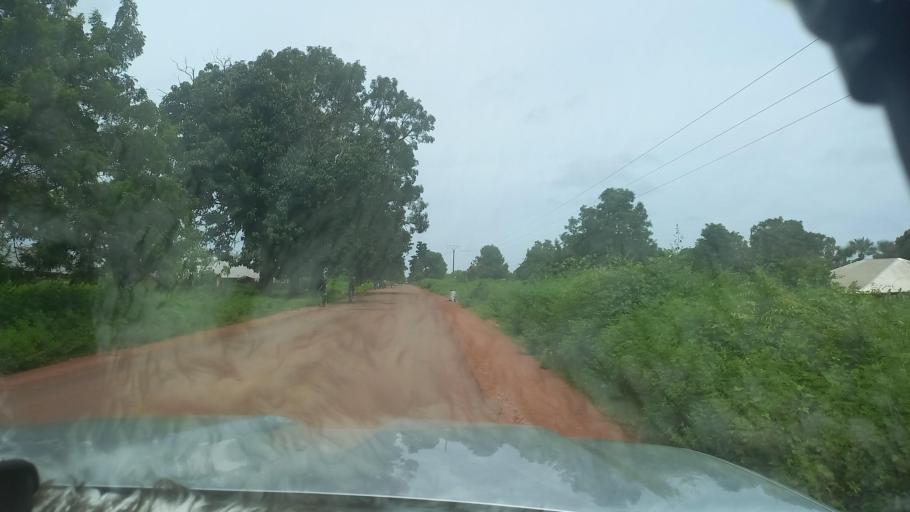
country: SN
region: Kolda
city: Marsassoum
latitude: 12.9166
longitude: -16.0096
